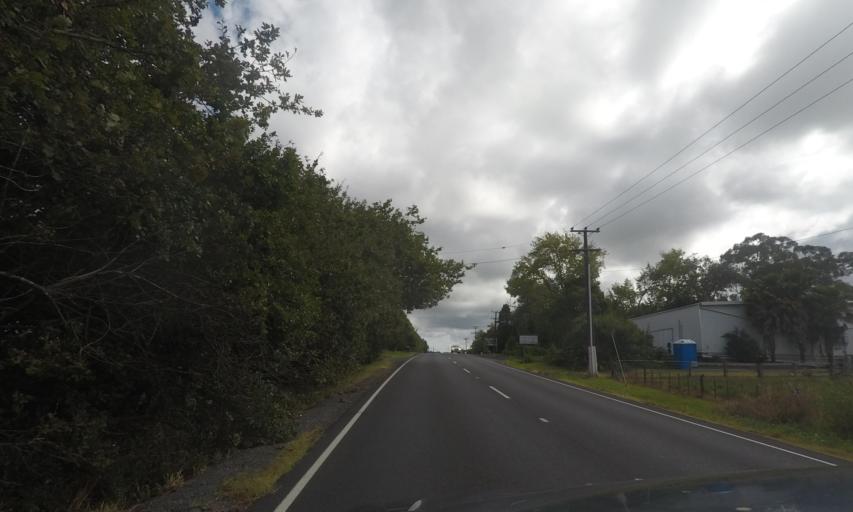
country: NZ
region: Auckland
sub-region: Auckland
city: Rosebank
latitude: -36.7954
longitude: 174.6017
